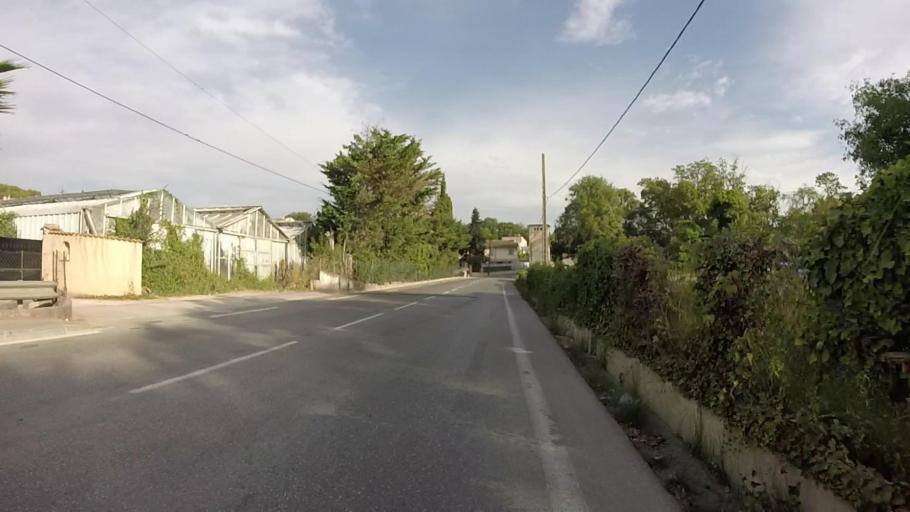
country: FR
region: Provence-Alpes-Cote d'Azur
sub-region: Departement des Alpes-Maritimes
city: Biot
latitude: 43.6088
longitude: 7.1107
